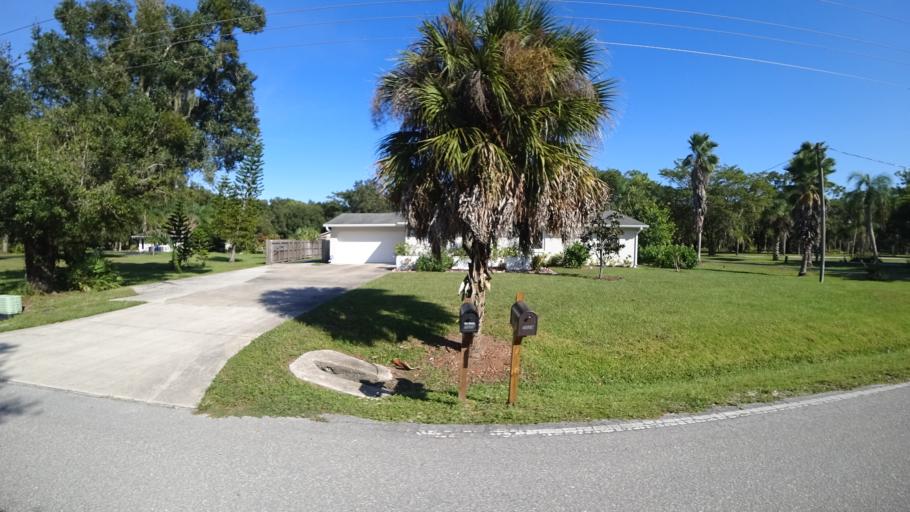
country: US
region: Florida
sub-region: Sarasota County
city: The Meadows
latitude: 27.4146
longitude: -82.4486
